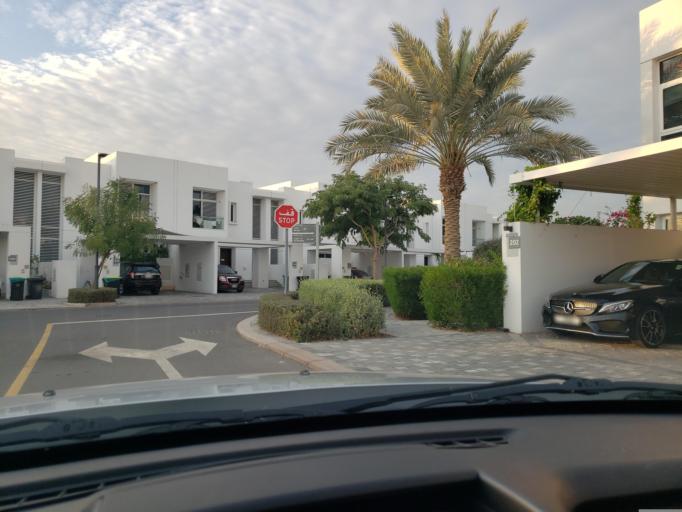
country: AE
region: Dubai
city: Dubai
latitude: 25.0164
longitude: 55.2709
